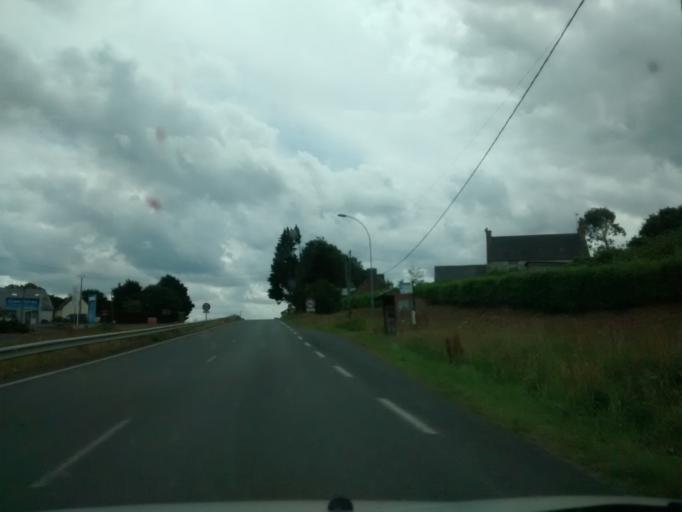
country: FR
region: Brittany
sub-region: Departement des Cotes-d'Armor
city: Saint-Quay-Perros
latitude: 48.7814
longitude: -3.4493
